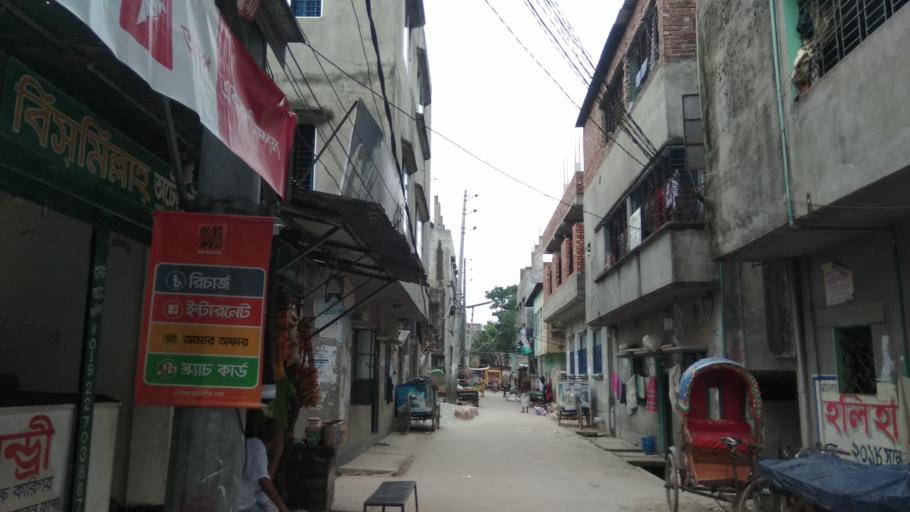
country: BD
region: Dhaka
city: Tungi
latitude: 23.8182
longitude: 90.3788
